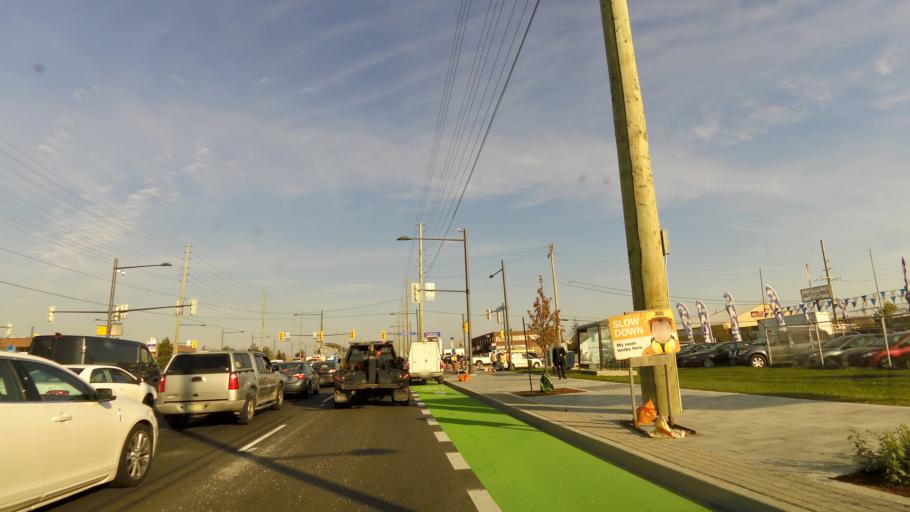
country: CA
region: Ontario
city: Concord
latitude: 43.7954
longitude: -79.5184
